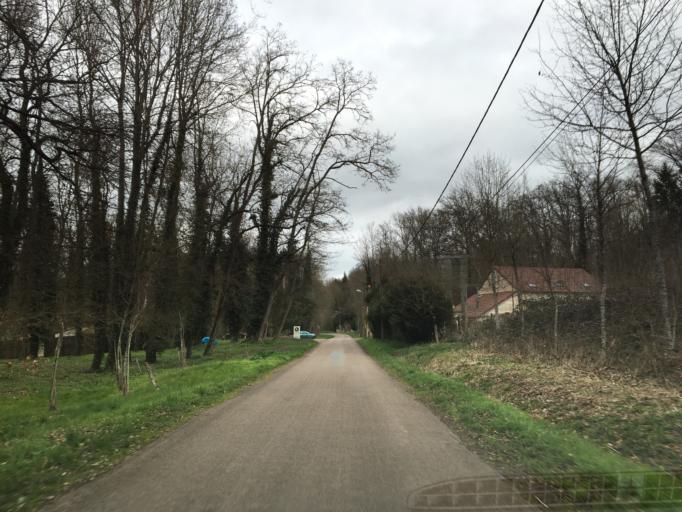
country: FR
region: Bourgogne
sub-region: Departement de l'Yonne
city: Fleury-la-Vallee
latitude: 47.8512
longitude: 3.3998
